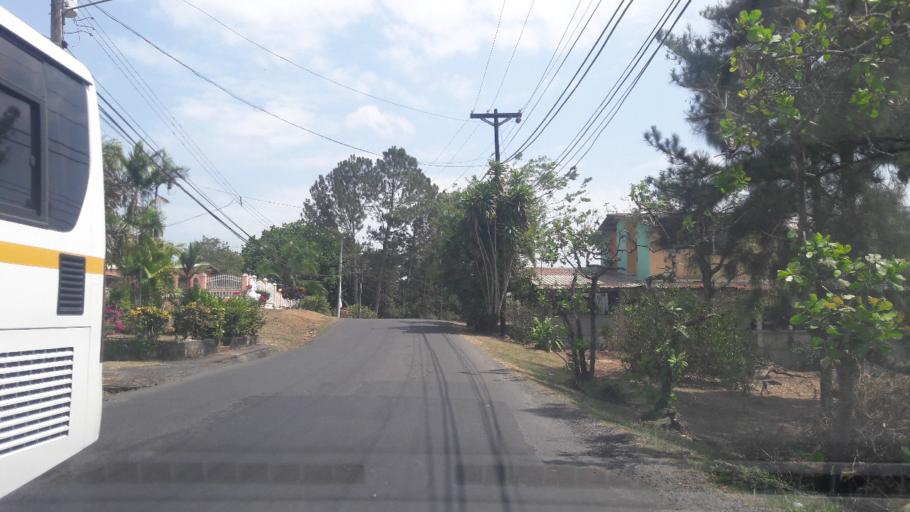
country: PA
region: Panama
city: Alcalde Diaz
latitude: 9.1357
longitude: -79.5520
